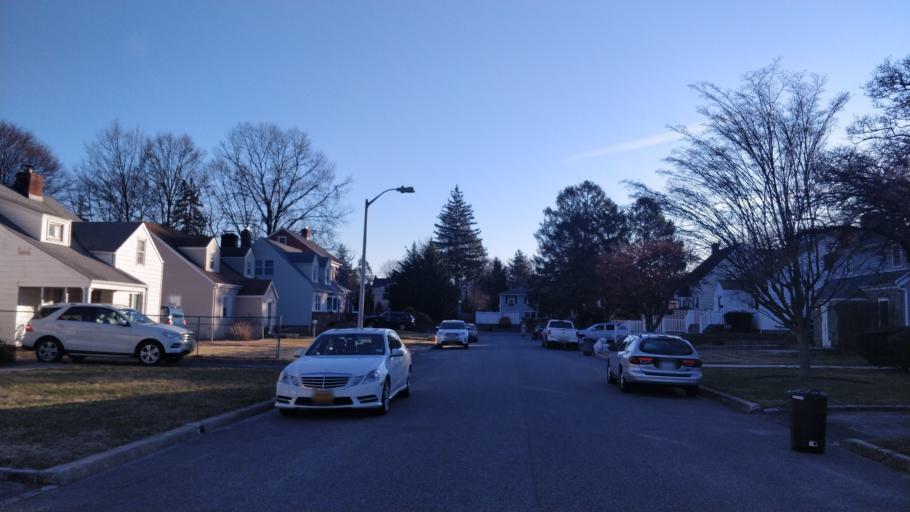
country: US
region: New York
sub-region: Nassau County
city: Glen Cove
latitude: 40.8704
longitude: -73.6373
